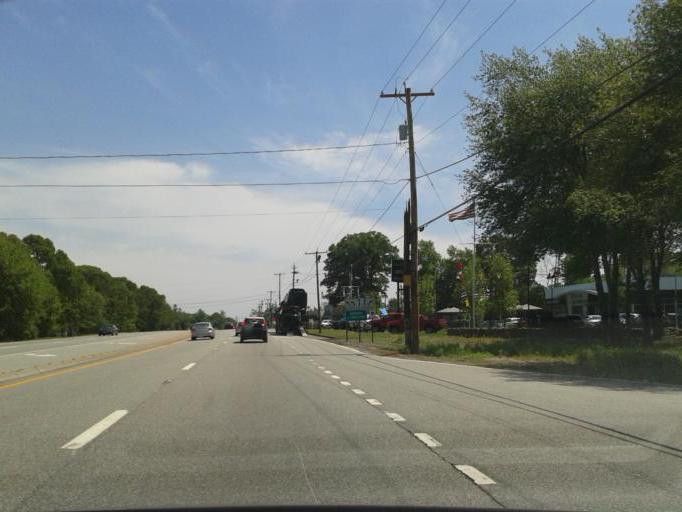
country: US
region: Rhode Island
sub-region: Washington County
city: North Kingstown
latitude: 41.4998
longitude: -71.4584
